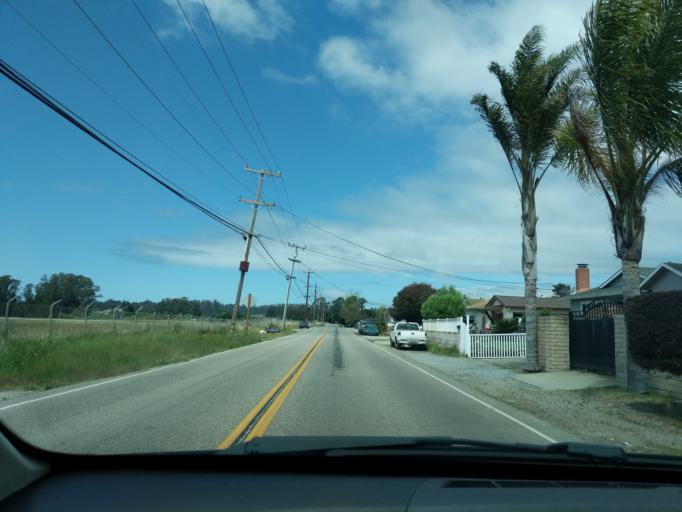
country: US
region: California
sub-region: Santa Cruz County
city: Freedom
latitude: 36.9396
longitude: -121.7900
